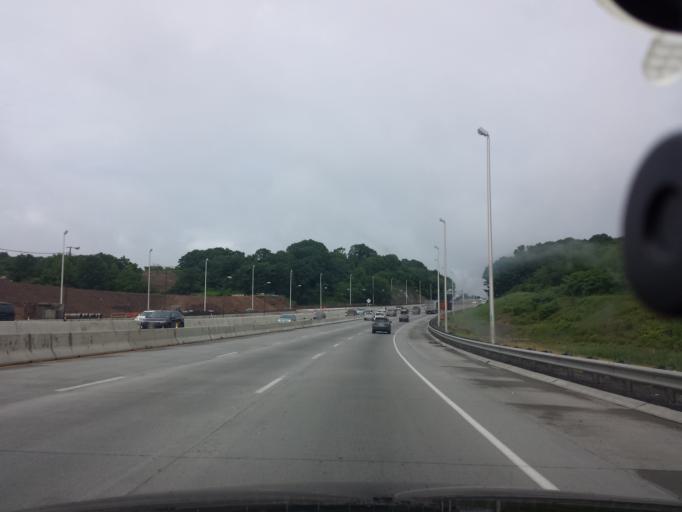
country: US
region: New York
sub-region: Richmond County
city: Staten Island
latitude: 40.6105
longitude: -74.1079
